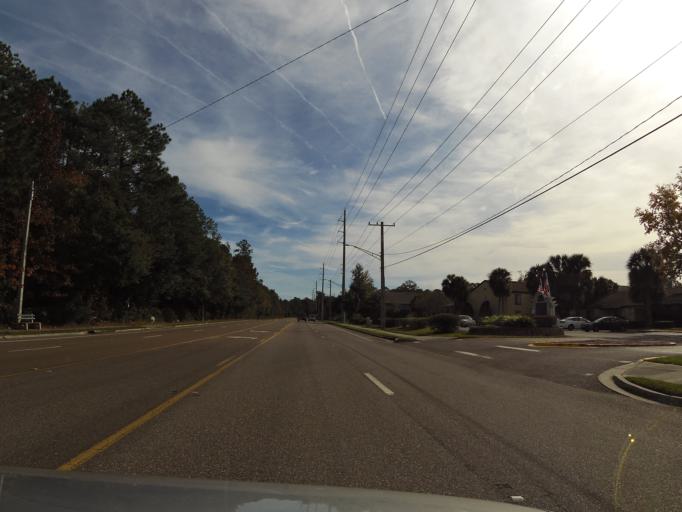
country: US
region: Florida
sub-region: Duval County
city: Jacksonville
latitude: 30.2474
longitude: -81.6119
